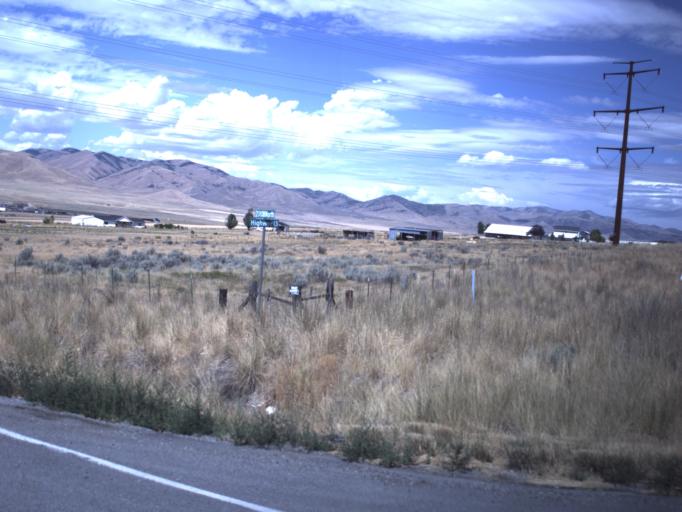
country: US
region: Utah
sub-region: Box Elder County
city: Garland
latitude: 41.8864
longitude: -112.1606
